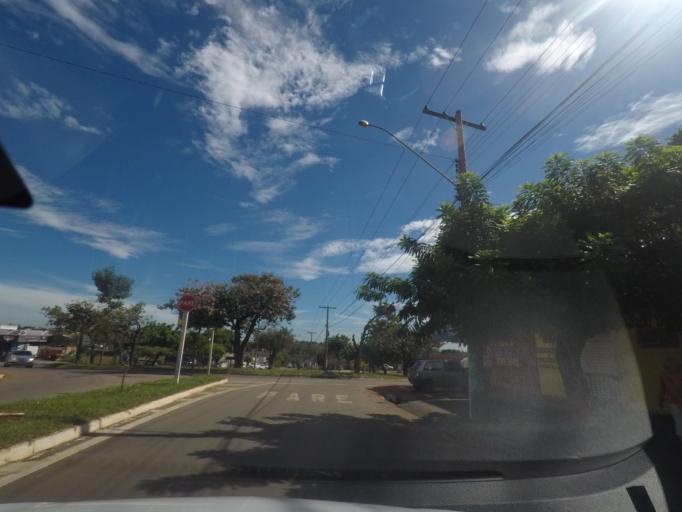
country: BR
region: Goias
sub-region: Aparecida De Goiania
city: Aparecida de Goiania
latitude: -16.7966
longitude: -49.2799
